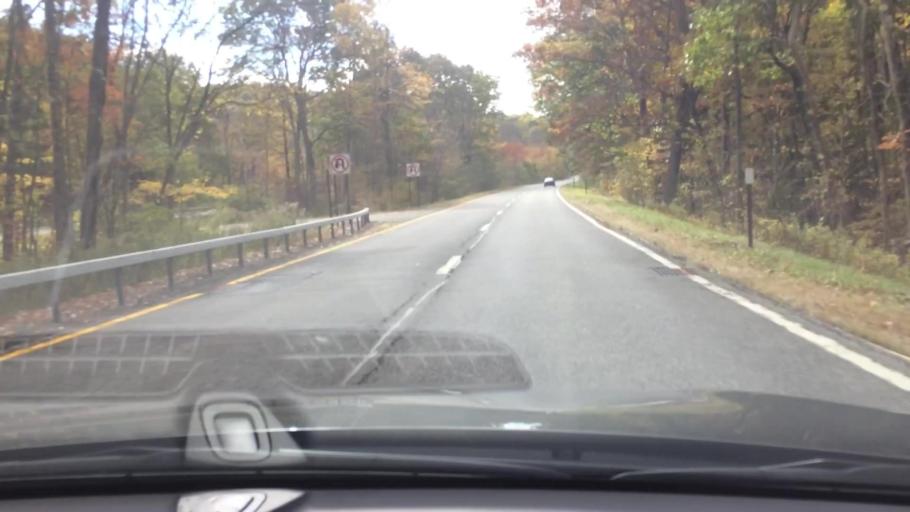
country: US
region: New York
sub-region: Dutchess County
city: Pine Plains
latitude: 41.9394
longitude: -73.7540
